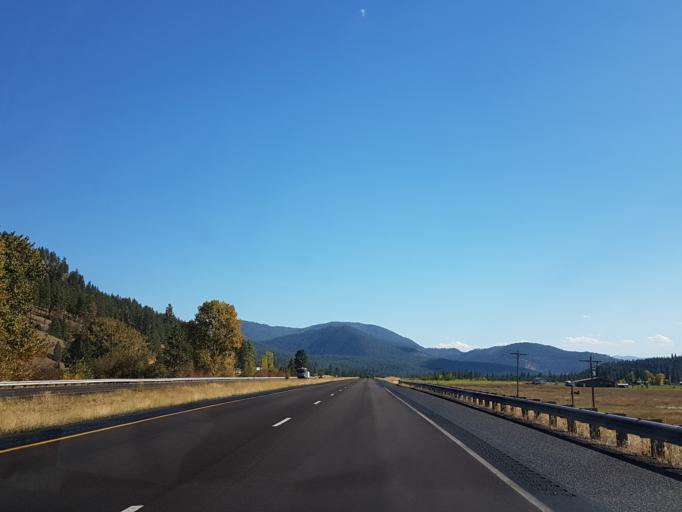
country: US
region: Montana
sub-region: Mineral County
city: Superior
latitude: 47.1426
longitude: -114.8137
